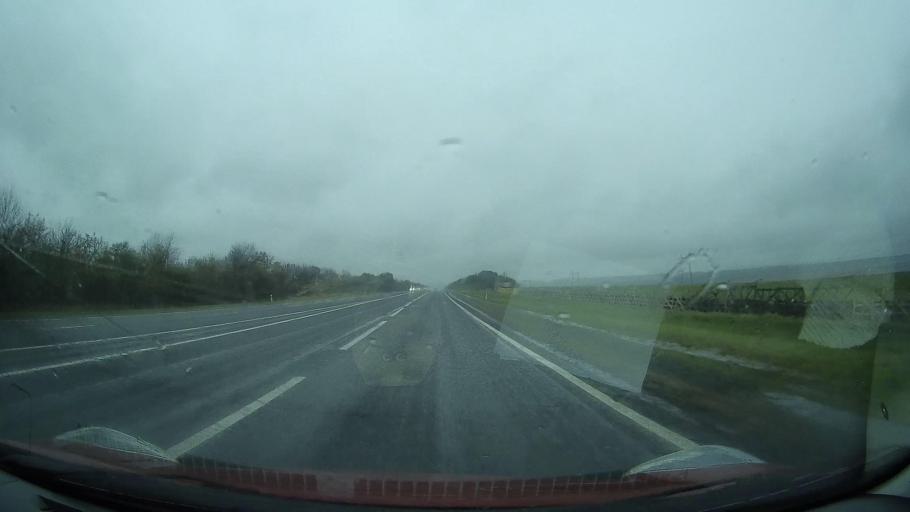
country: RU
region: Stavropol'skiy
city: Nevinnomyssk
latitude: 44.6148
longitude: 42.1098
